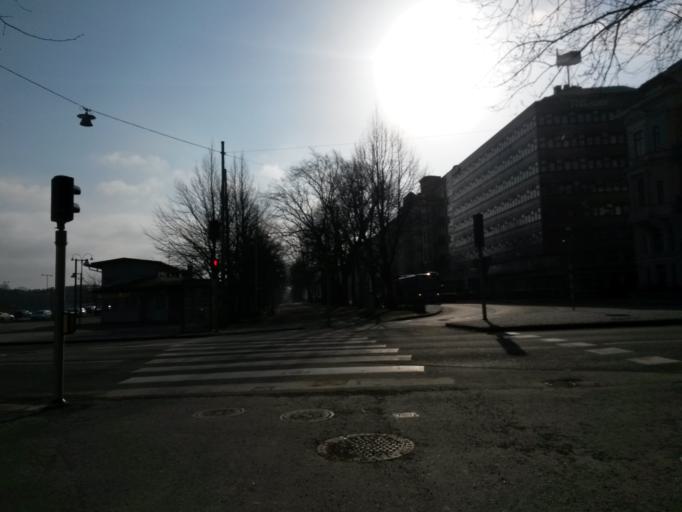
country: SE
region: Vaestra Goetaland
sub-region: Goteborg
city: Goeteborg
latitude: 57.7027
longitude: 11.9739
